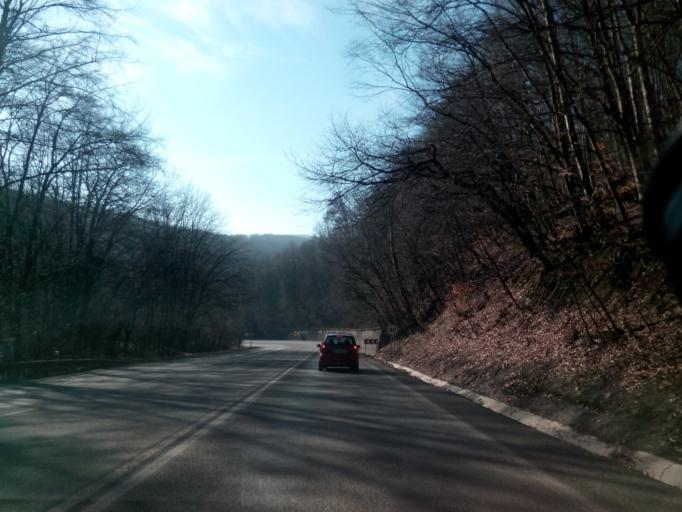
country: SK
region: Kosicky
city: Secovce
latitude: 48.7347
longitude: 21.5375
